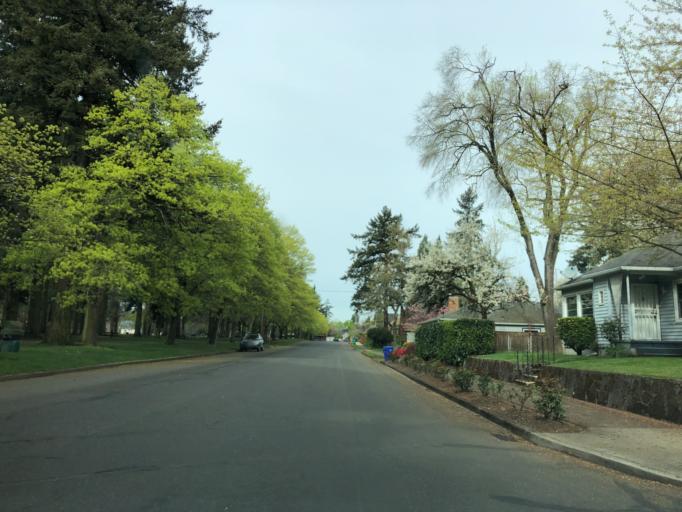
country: US
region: Oregon
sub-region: Multnomah County
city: Portland
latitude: 45.5537
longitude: -122.6266
